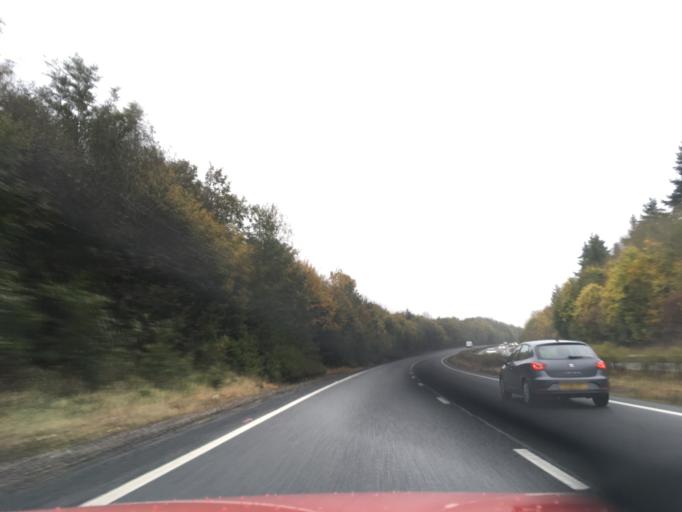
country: GB
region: England
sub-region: Hampshire
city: Highclere
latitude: 51.3386
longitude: -1.3408
